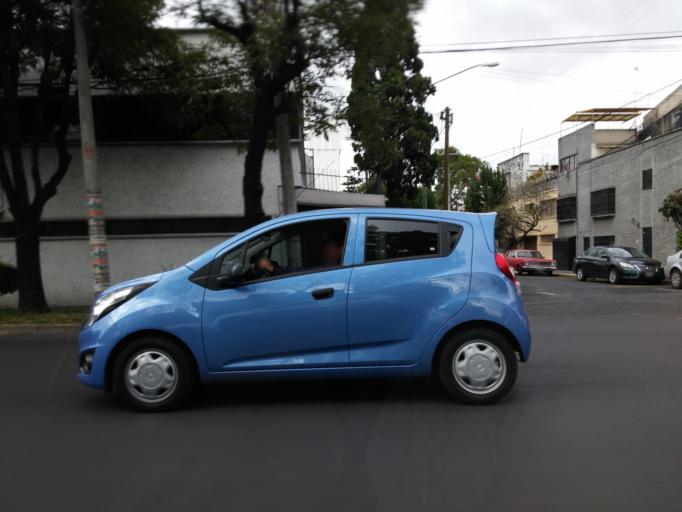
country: MX
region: Mexico City
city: Cuauhtemoc
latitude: 19.4605
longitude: -99.1680
